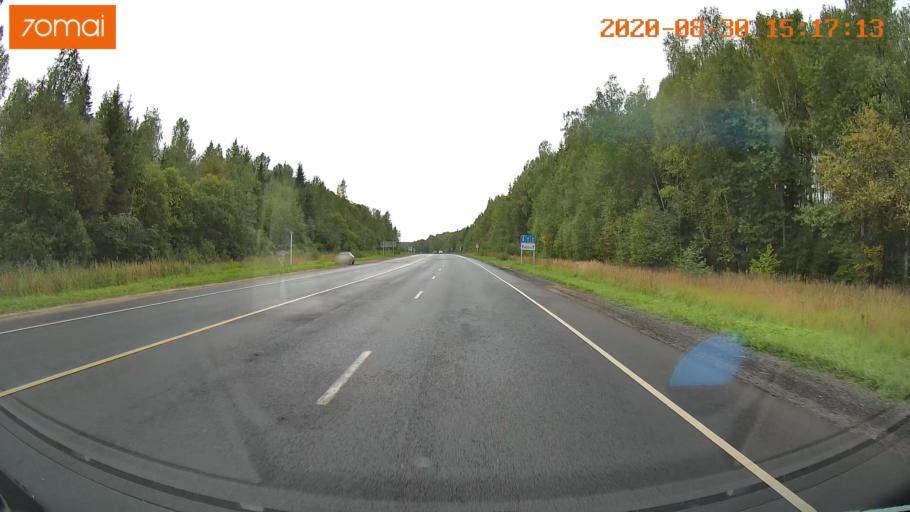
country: RU
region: Ivanovo
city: Rodniki
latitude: 57.1369
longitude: 41.8077
